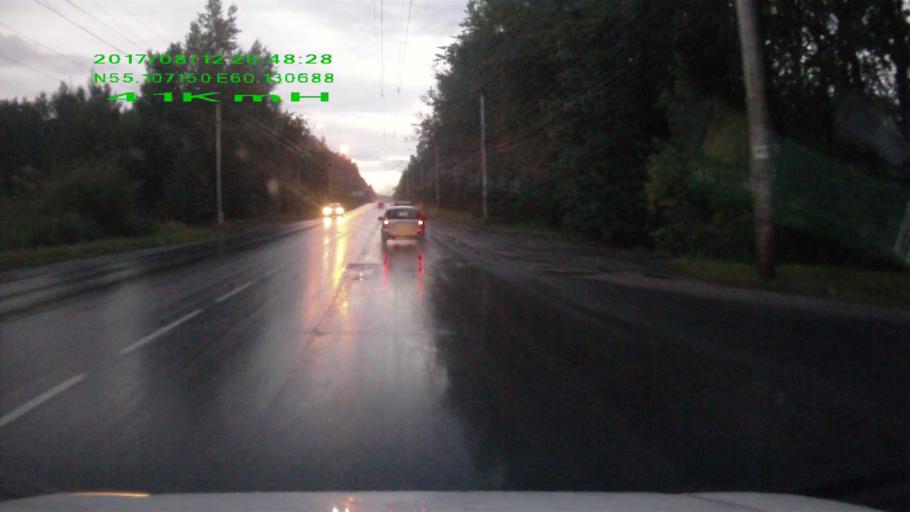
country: RU
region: Chelyabinsk
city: Turgoyak
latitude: 55.1072
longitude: 60.1307
